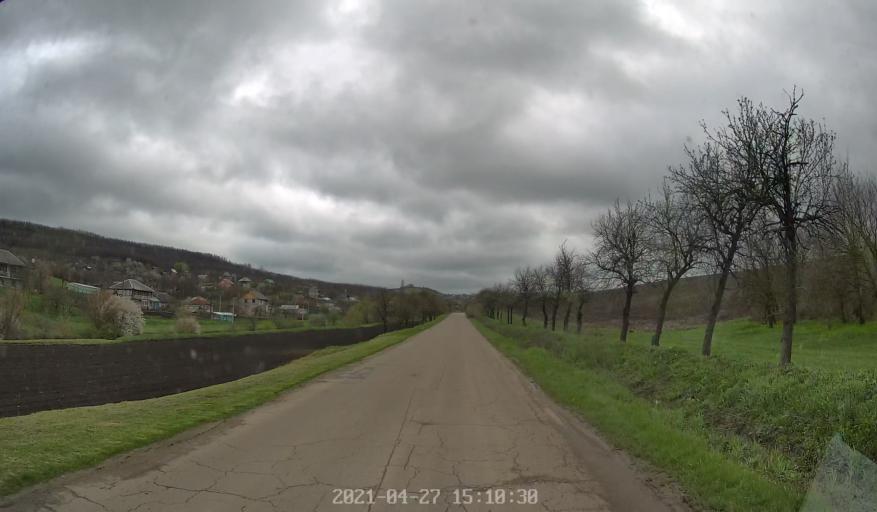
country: MD
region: Chisinau
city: Vadul lui Voda
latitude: 47.0398
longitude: 29.0326
